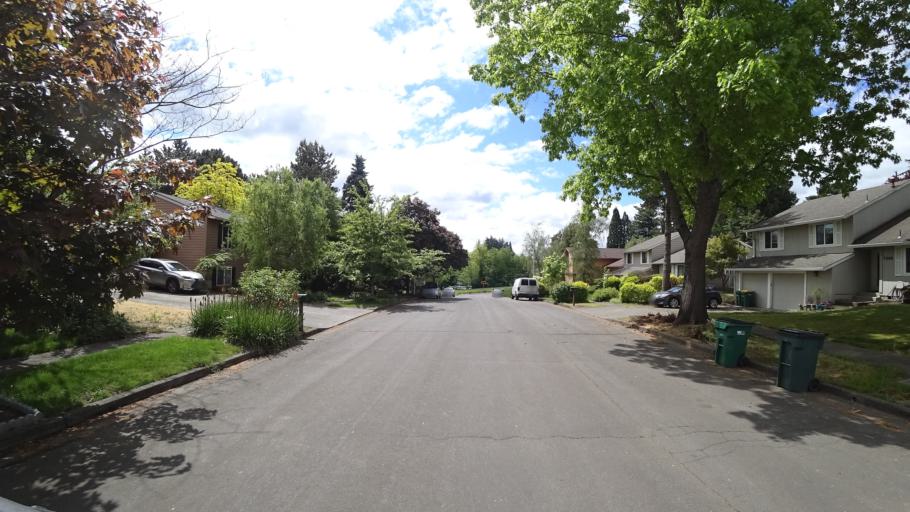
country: US
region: Oregon
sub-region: Washington County
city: Beaverton
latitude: 45.4673
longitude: -122.8027
